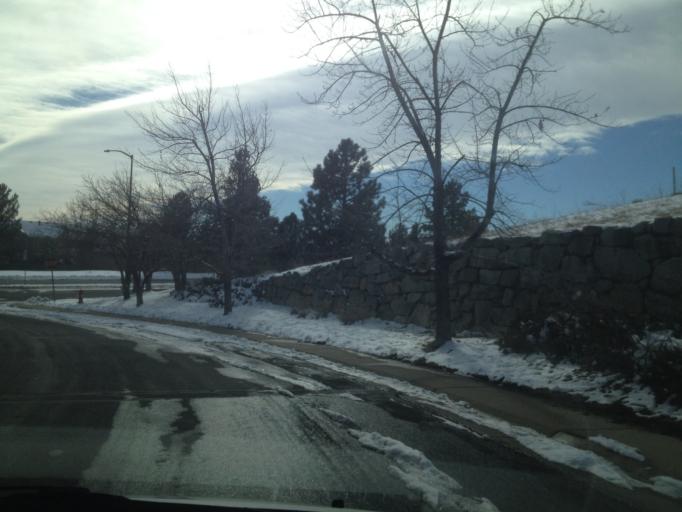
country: US
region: Colorado
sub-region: Boulder County
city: Louisville
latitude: 39.9773
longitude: -105.1541
